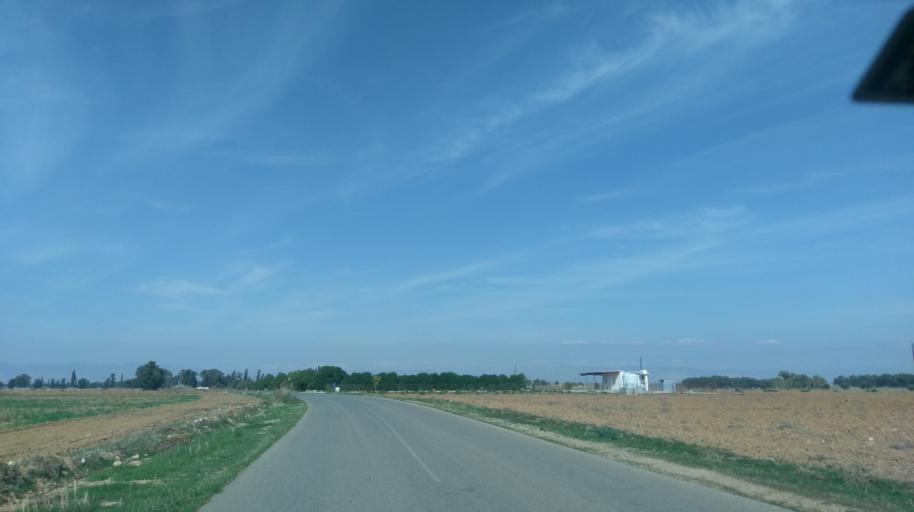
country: CY
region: Larnaka
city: Pergamos
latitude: 35.1205
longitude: 33.7256
